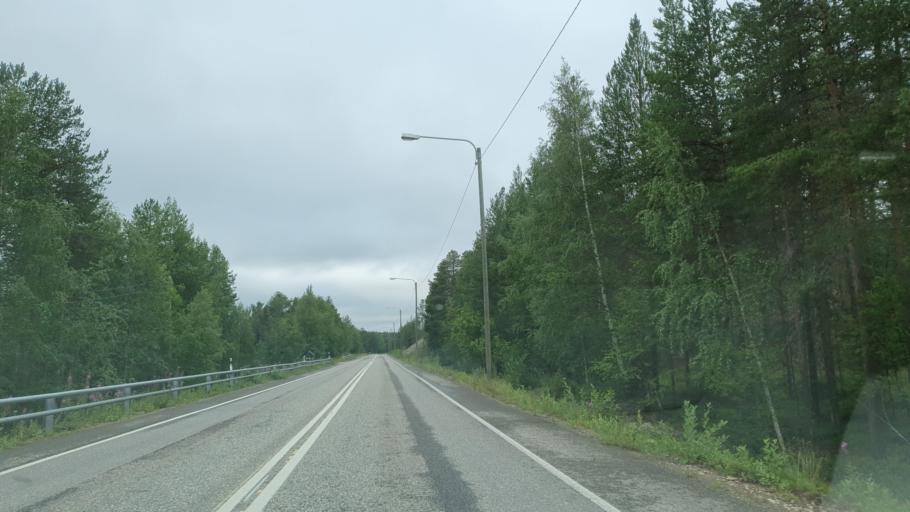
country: FI
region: Lapland
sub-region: Pohjois-Lappi
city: Sodankylae
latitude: 67.3739
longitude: 26.8781
